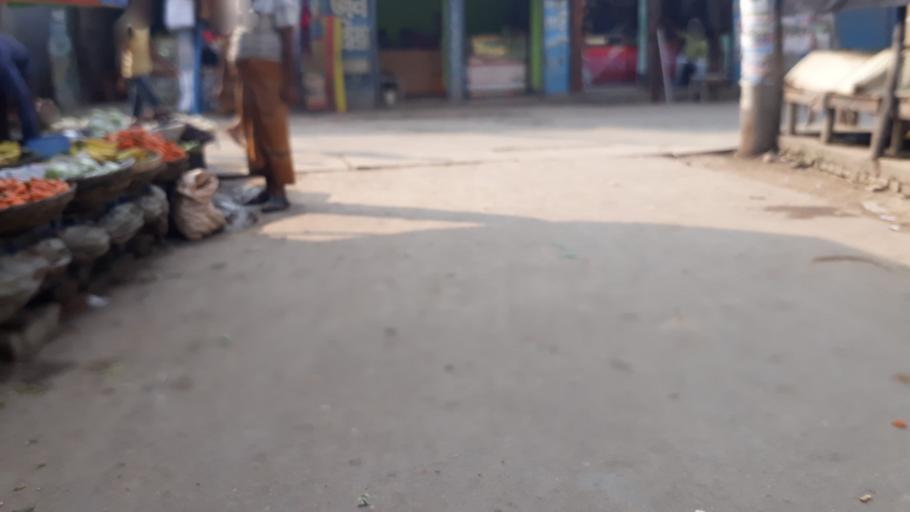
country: BD
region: Khulna
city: Kaliganj
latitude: 23.3560
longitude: 88.9148
